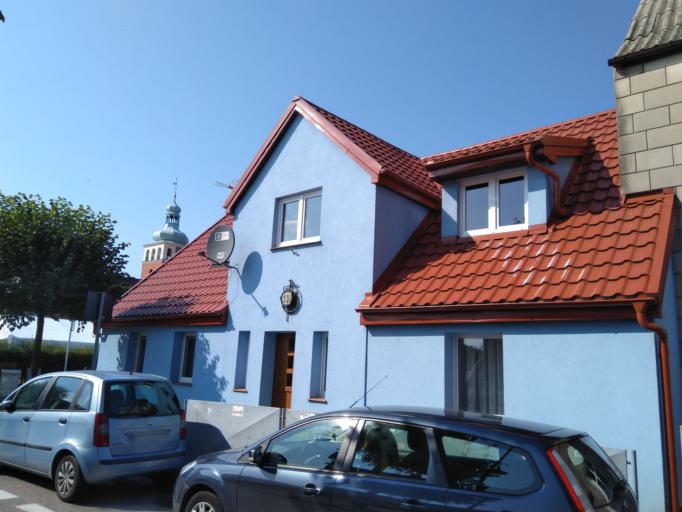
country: PL
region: Pomeranian Voivodeship
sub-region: Powiat pucki
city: Jastarnia
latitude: 54.7021
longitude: 18.6727
